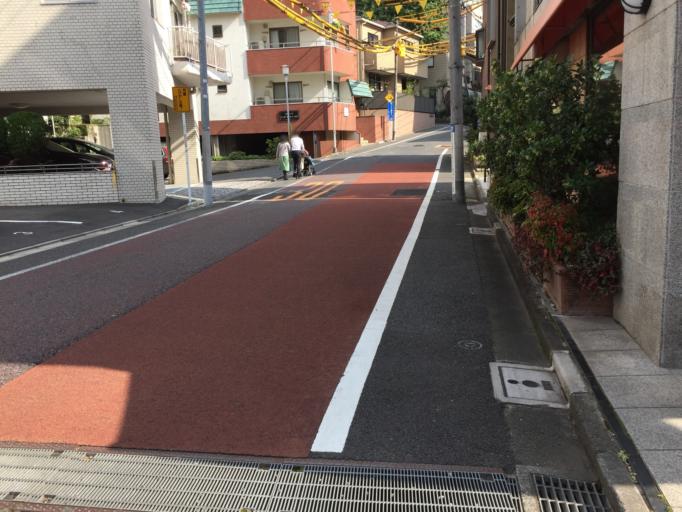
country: JP
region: Tokyo
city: Tokyo
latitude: 35.6414
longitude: 139.7196
